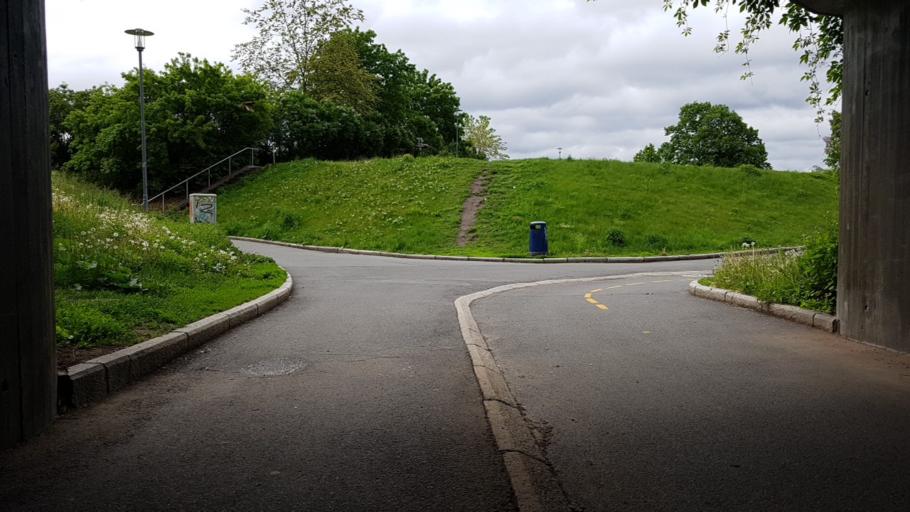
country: NO
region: Oslo
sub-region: Oslo
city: Oslo
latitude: 59.9309
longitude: 10.7718
